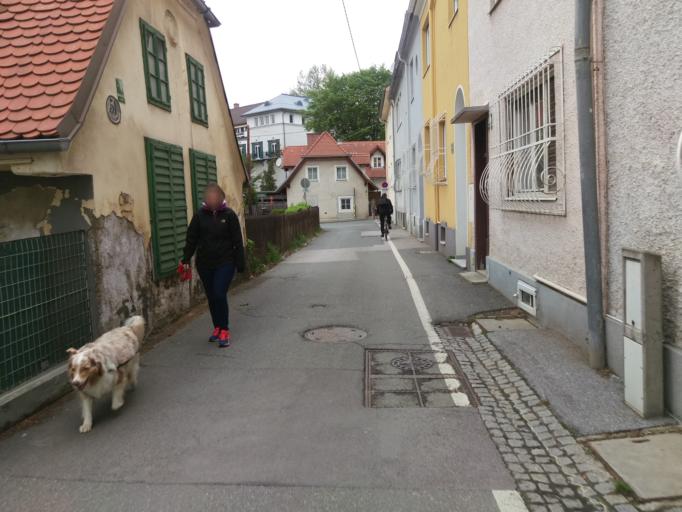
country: AT
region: Styria
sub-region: Graz Stadt
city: Graz
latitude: 47.0827
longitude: 15.4462
